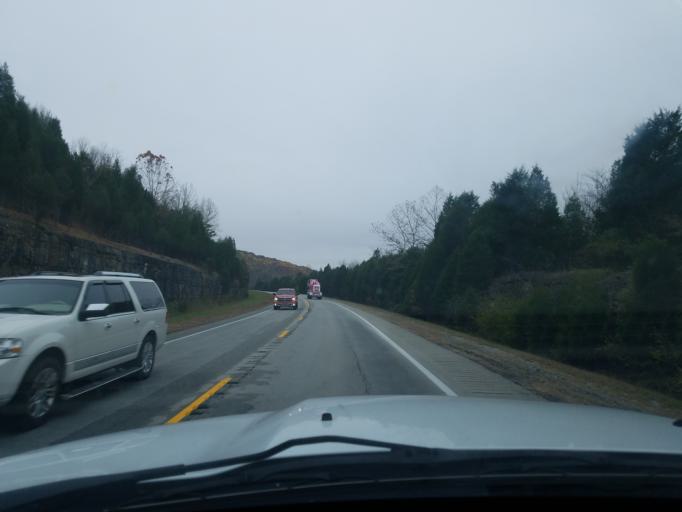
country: US
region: Kentucky
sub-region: Bullitt County
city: Shepherdsville
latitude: 37.9245
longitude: -85.6289
